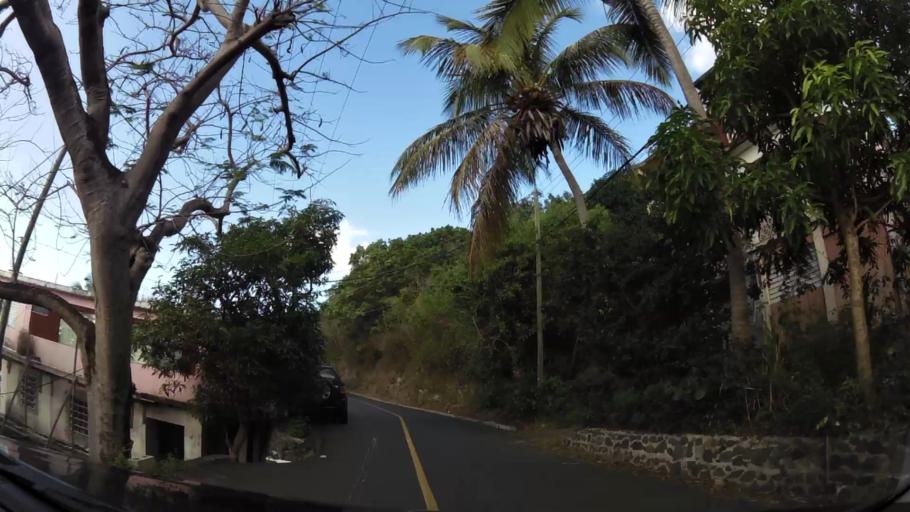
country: VG
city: Road Town
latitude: 18.4027
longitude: -64.6765
